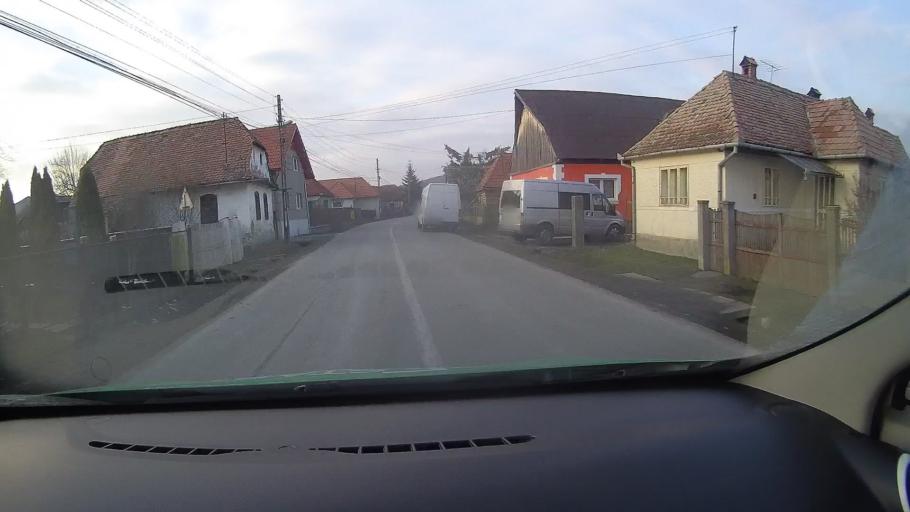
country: RO
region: Harghita
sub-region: Oras Cristuru Secuiesc
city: Cristuru Secuiesc
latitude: 46.3023
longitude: 25.0695
